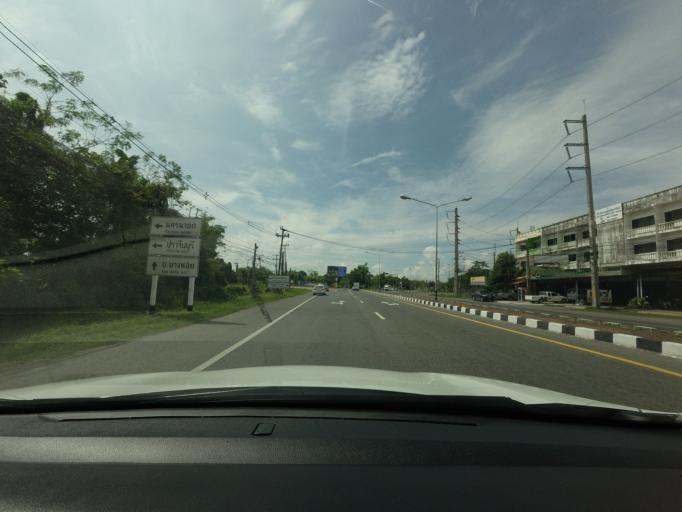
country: TH
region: Nakhon Nayok
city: Nakhon Nayok
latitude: 14.1999
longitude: 101.1926
